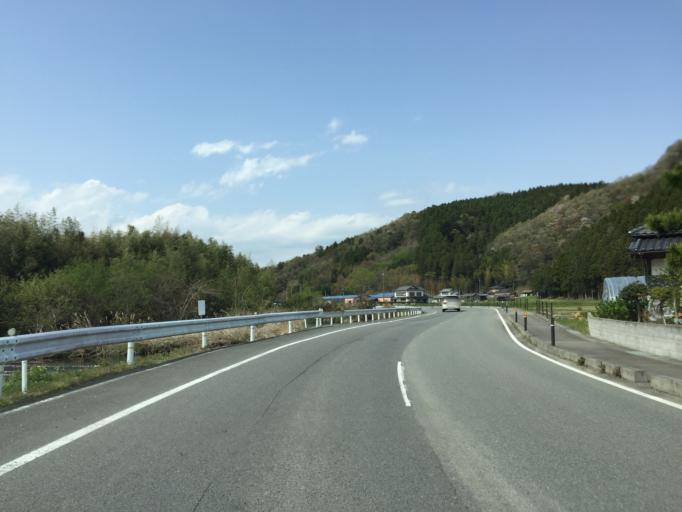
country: JP
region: Fukushima
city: Iwaki
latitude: 37.1529
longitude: 140.9843
